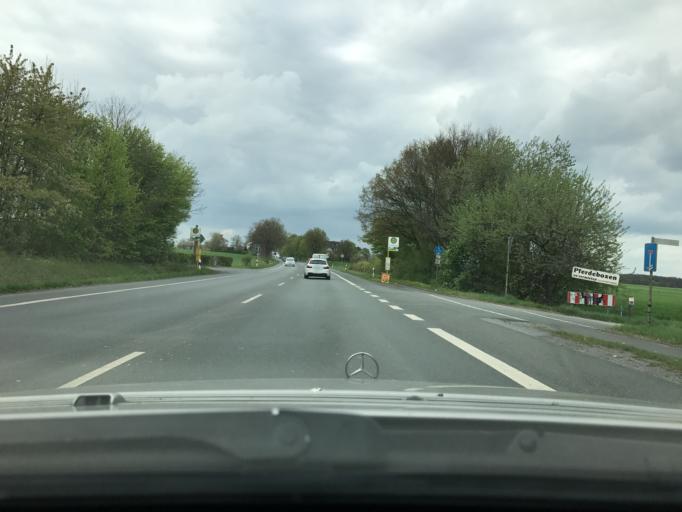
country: DE
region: North Rhine-Westphalia
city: Waltrop
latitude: 51.5966
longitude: 7.3934
